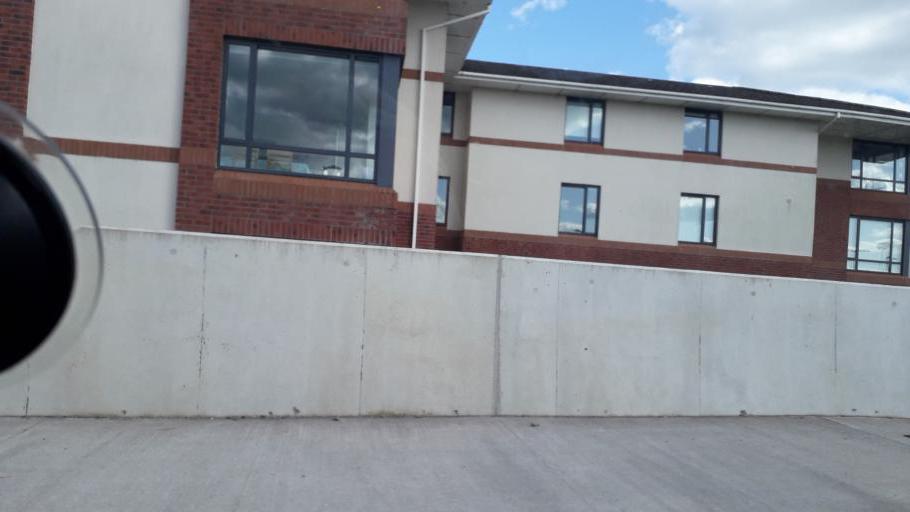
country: IE
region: Leinster
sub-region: Kildare
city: Maynooth
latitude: 53.3870
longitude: -6.6010
